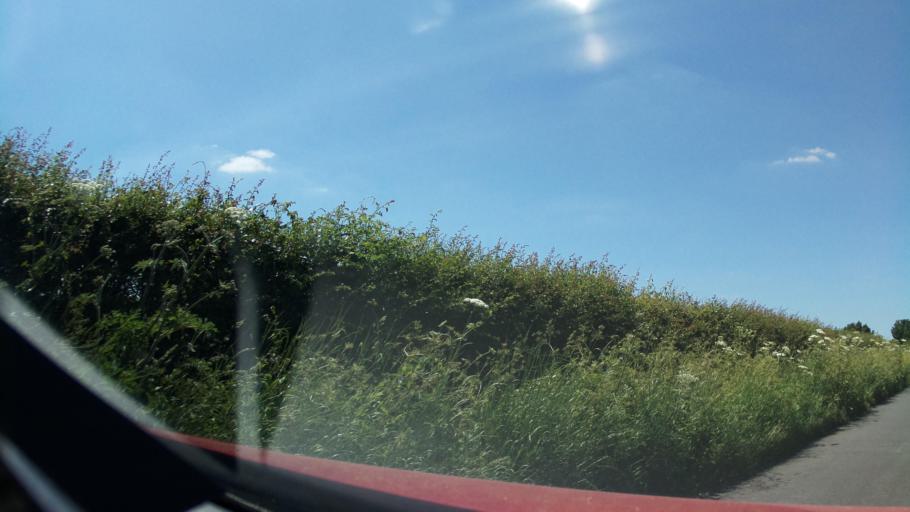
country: GB
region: England
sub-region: Wiltshire
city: Royal Wootton Bassett
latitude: 51.5157
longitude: -1.8958
